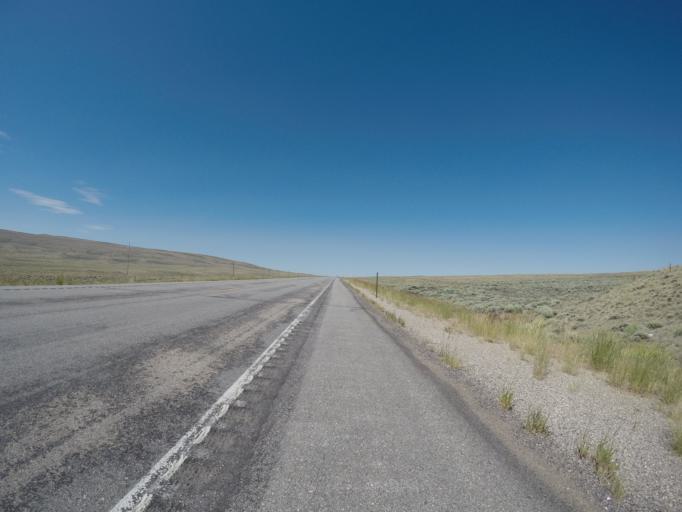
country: US
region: Wyoming
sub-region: Carbon County
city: Saratoga
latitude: 41.7996
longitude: -106.7129
